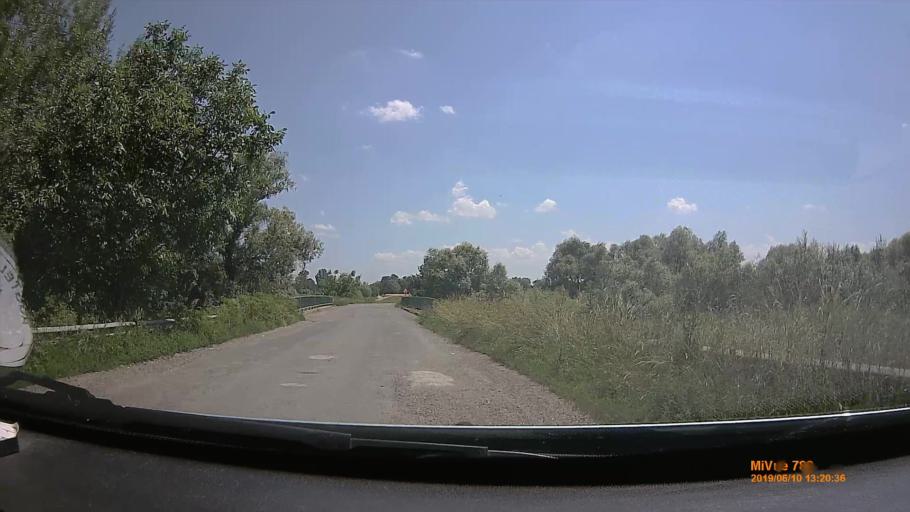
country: HU
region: Borsod-Abauj-Zemplen
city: Tiszaluc
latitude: 48.0398
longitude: 21.0794
